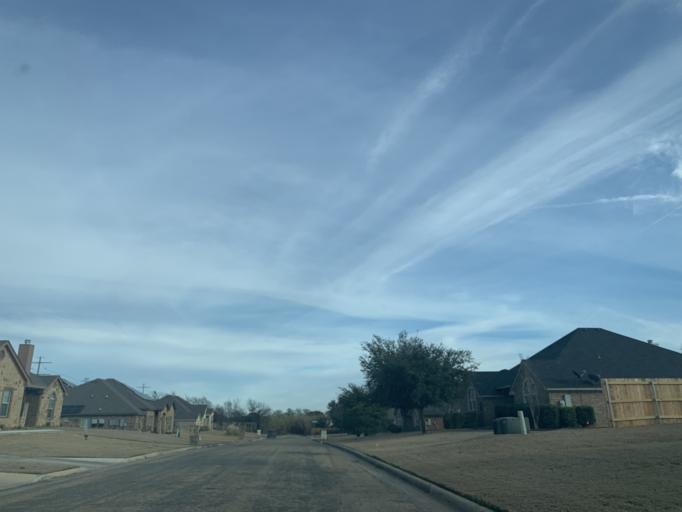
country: US
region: Texas
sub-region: Bell County
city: Salado
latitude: 30.9697
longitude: -97.5116
